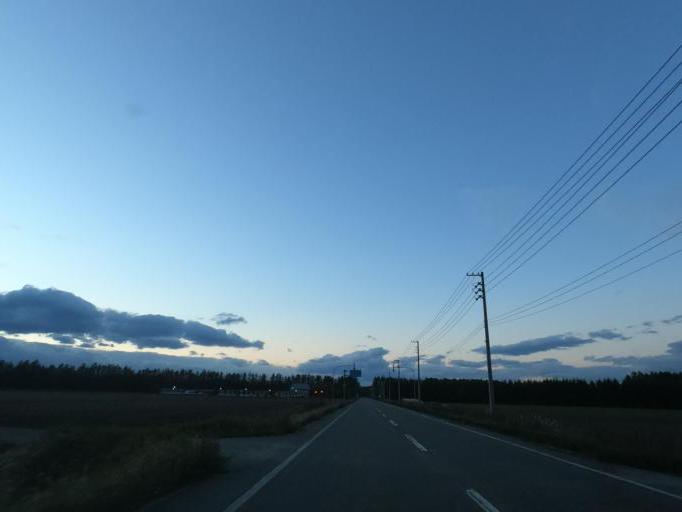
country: JP
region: Hokkaido
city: Obihiro
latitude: 42.6705
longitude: 143.1710
